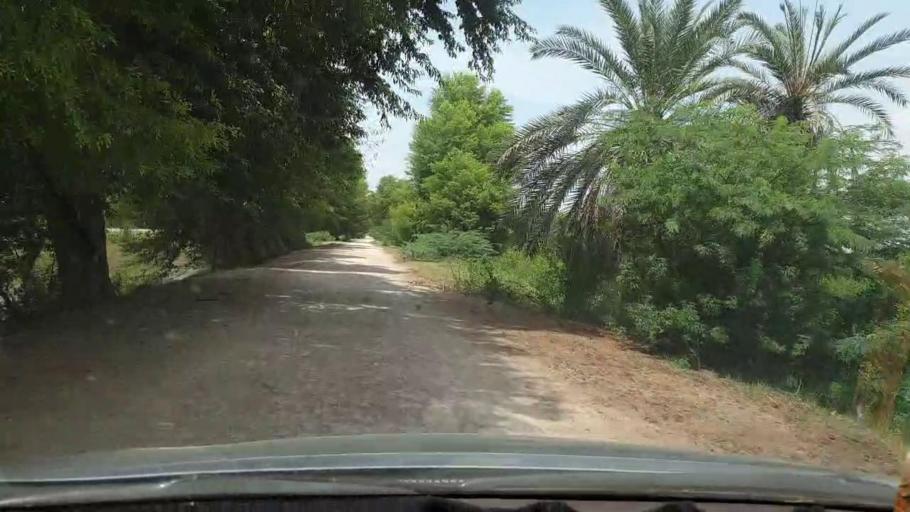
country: PK
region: Sindh
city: Khairpur
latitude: 27.4658
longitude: 68.8049
